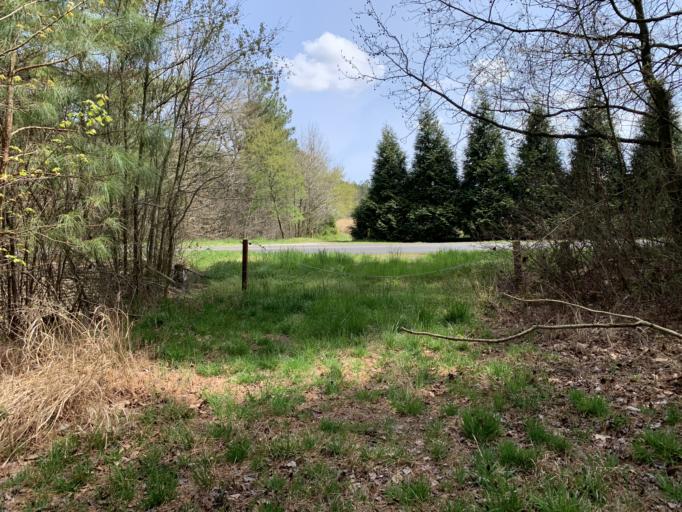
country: US
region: Delaware
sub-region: Sussex County
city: Millsboro
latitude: 38.5384
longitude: -75.3851
